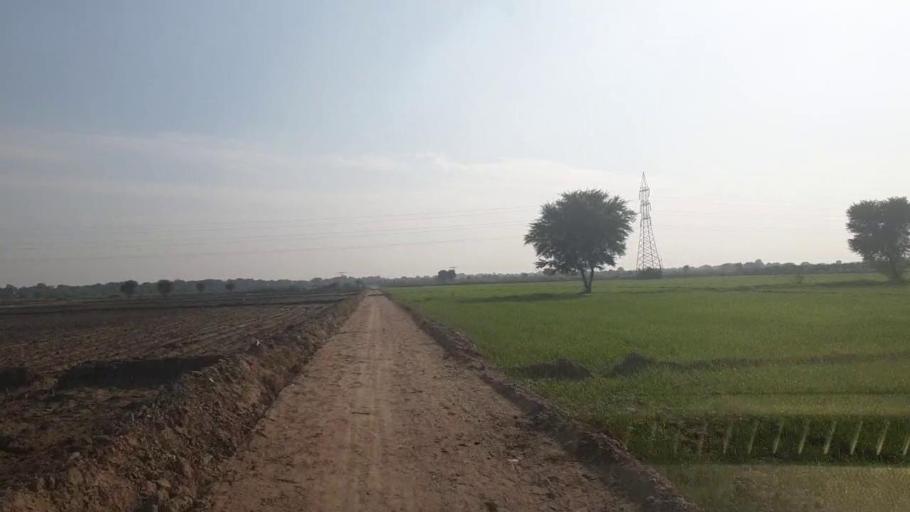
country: PK
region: Sindh
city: Tando Jam
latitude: 25.4286
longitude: 68.4771
